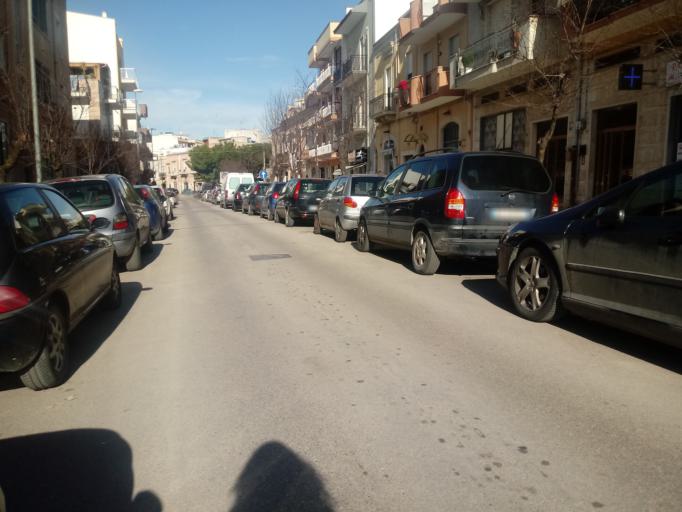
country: IT
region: Apulia
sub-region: Provincia di Barletta - Andria - Trani
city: Andria
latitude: 41.2207
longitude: 16.2999
